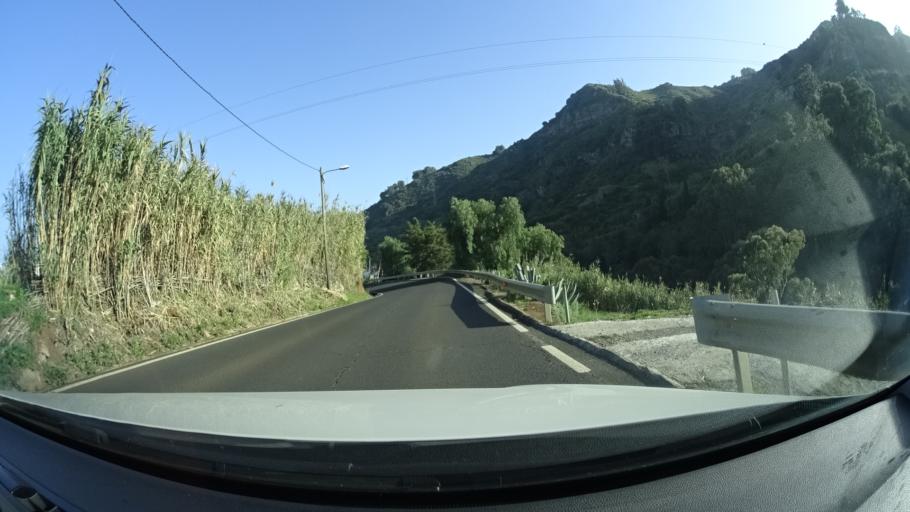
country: ES
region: Canary Islands
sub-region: Provincia de Las Palmas
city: Teror
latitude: 28.0585
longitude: -15.5560
